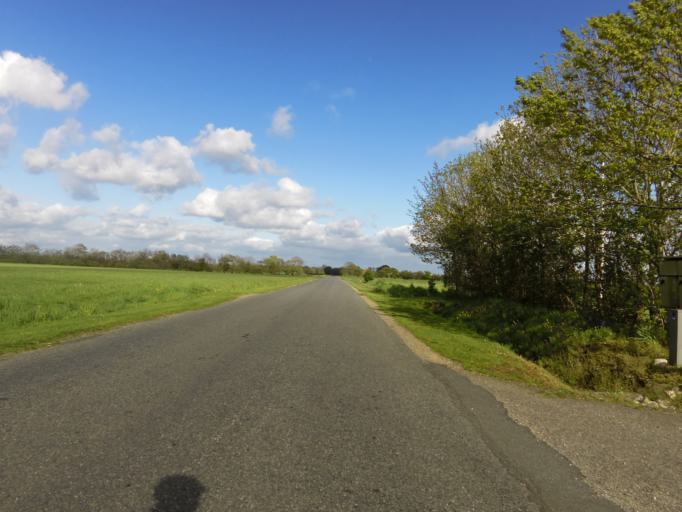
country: DK
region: South Denmark
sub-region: Esbjerg Kommune
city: Ribe
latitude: 55.2583
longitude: 8.8090
